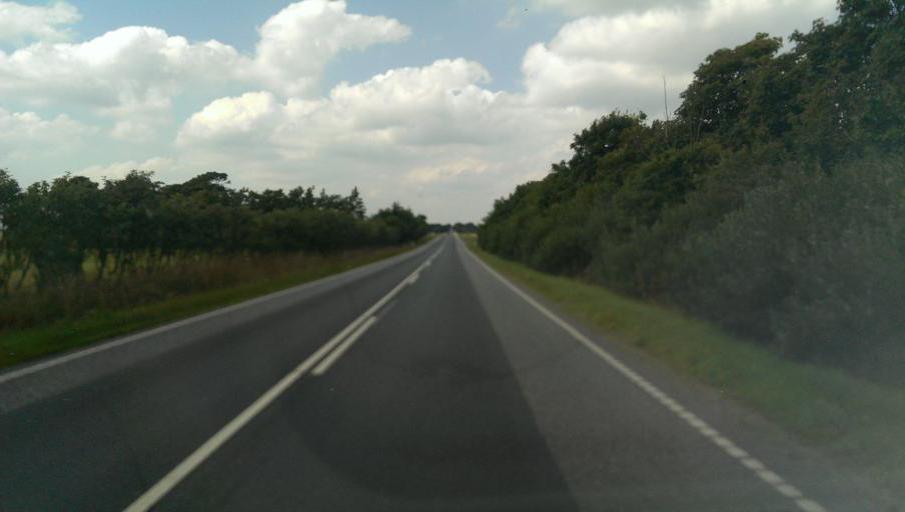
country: DK
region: South Denmark
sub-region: Esbjerg Kommune
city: Tjaereborg
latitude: 55.5371
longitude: 8.5783
